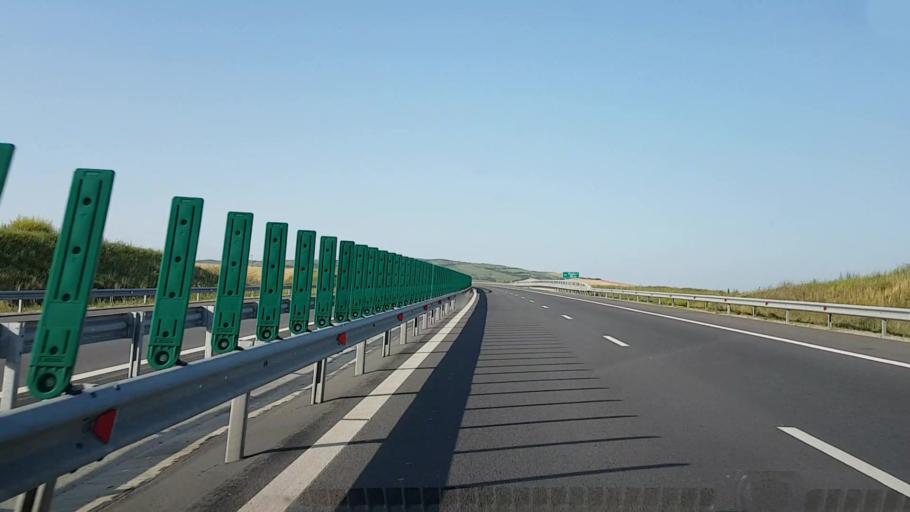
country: RO
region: Alba
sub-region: Comuna Unirea
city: Unirea
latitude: 46.3968
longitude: 23.7914
